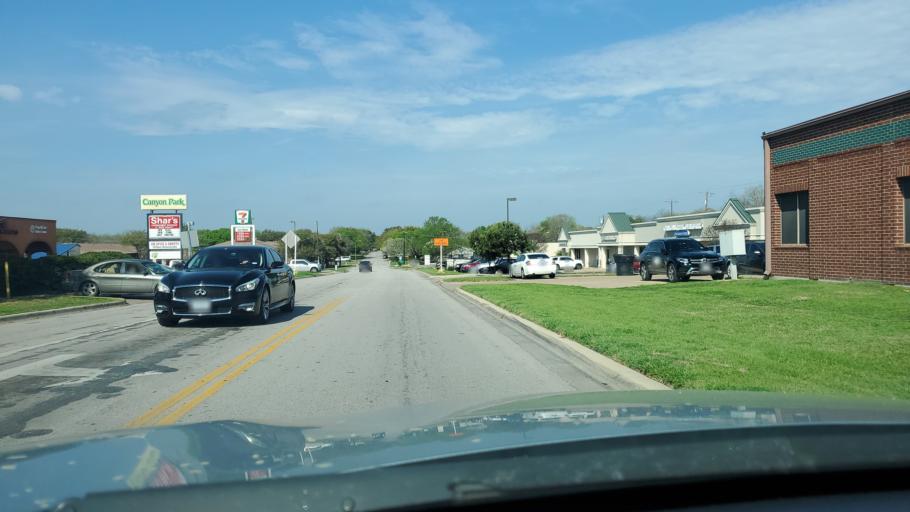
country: US
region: Texas
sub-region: Bell County
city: Temple
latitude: 31.0614
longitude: -97.3728
